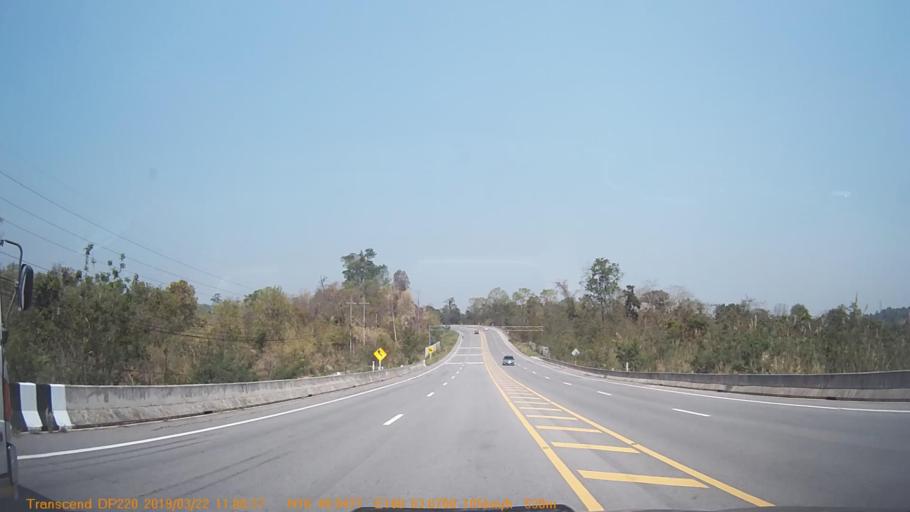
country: TH
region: Phetchabun
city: Khao Kho
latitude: 16.8327
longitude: 100.8943
